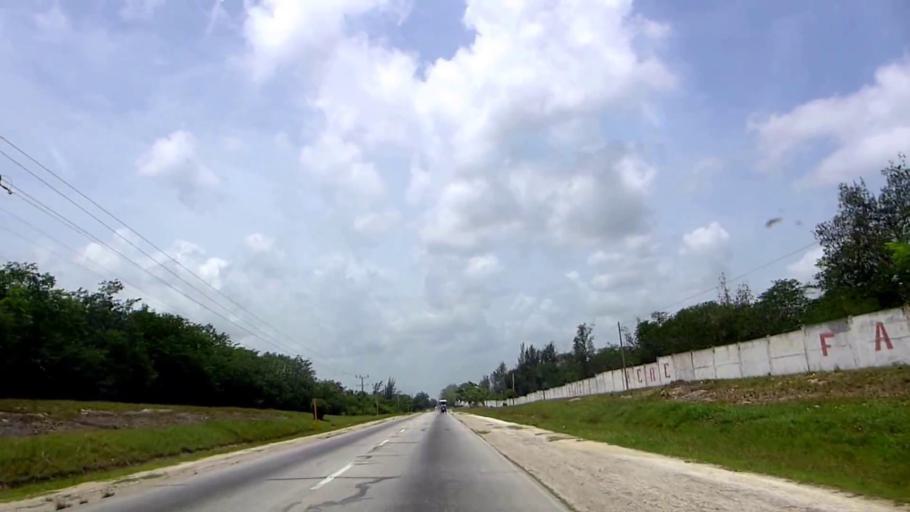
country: CU
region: Holguin
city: Cacocum
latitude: 20.7979
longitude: -76.2967
